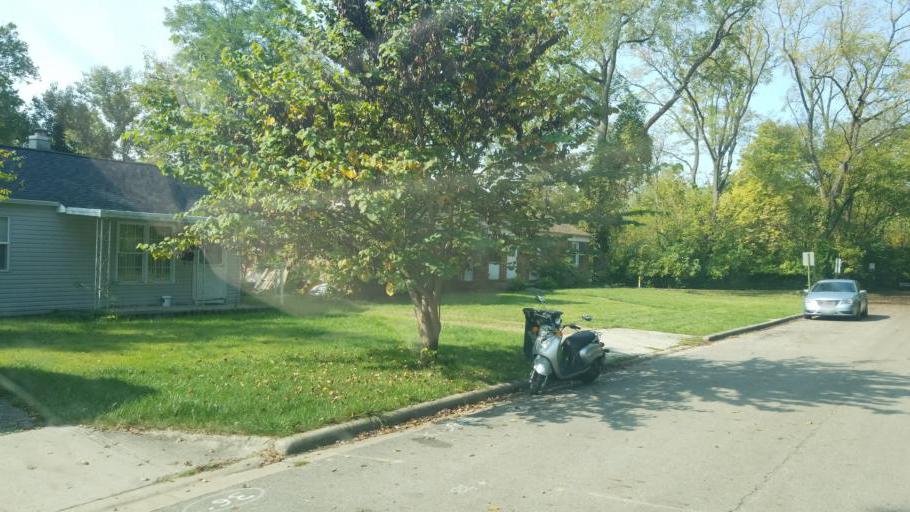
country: US
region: Ohio
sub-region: Franklin County
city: Worthington
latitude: 40.0726
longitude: -83.0333
